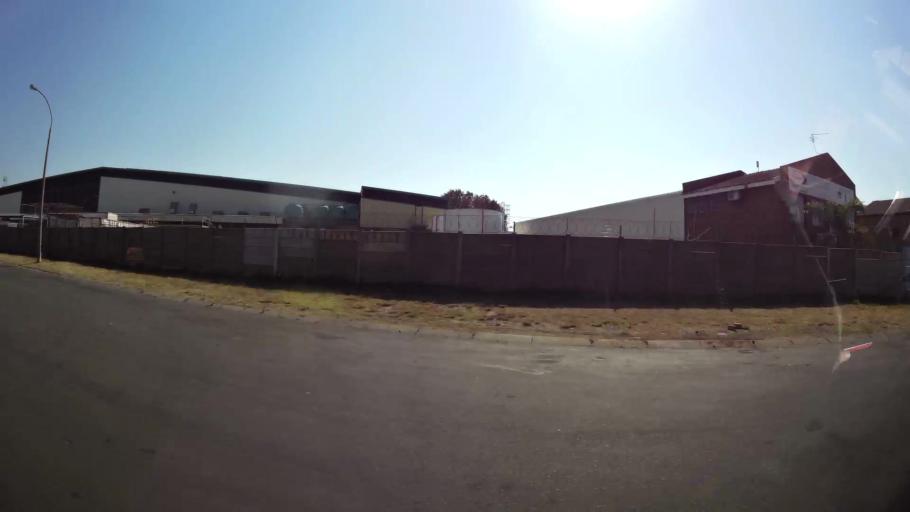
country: ZA
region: Gauteng
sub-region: Ekurhuleni Metropolitan Municipality
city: Boksburg
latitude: -26.1754
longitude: 28.2237
